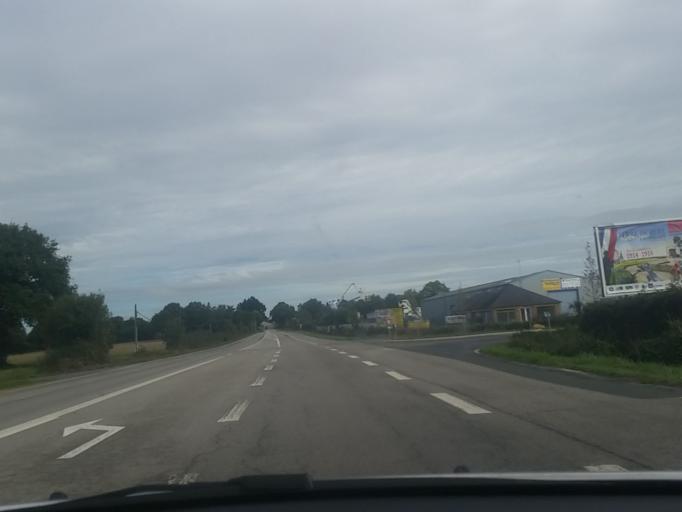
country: FR
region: Pays de la Loire
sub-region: Departement de la Loire-Atlantique
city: Chateaubriant
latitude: 47.7425
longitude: -1.3602
